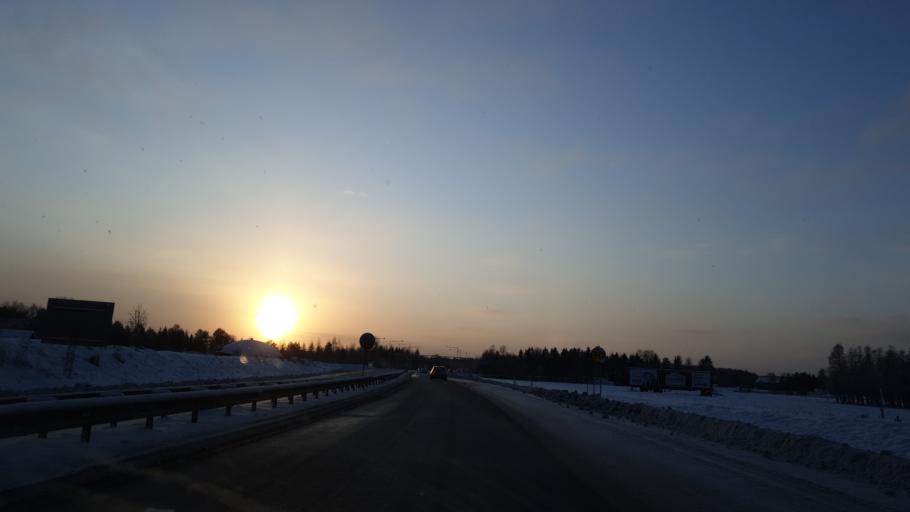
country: SE
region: Vaesterbotten
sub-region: Umea Kommun
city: Roback
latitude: 63.7804
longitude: 20.1923
